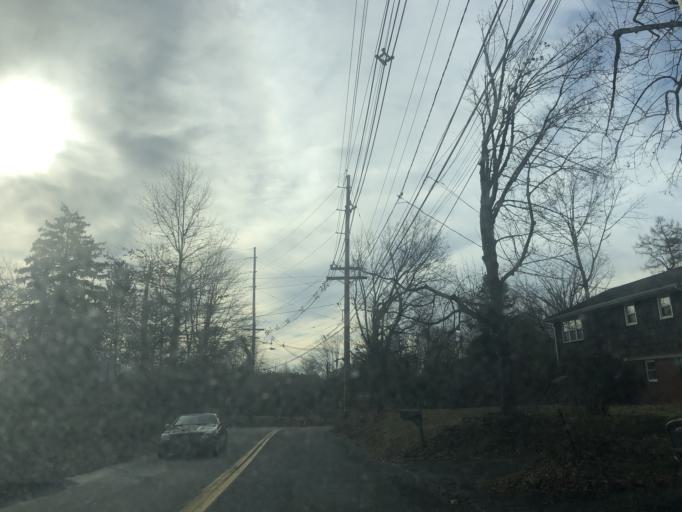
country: US
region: New Jersey
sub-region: Somerset County
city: Kingston
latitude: 40.3729
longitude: -74.6152
